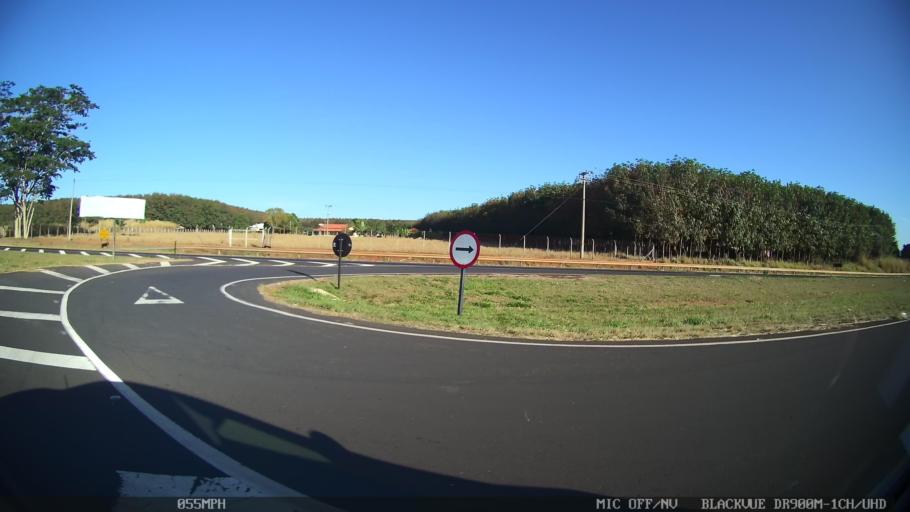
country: BR
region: Sao Paulo
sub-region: Guapiacu
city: Guapiacu
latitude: -20.7520
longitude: -49.1417
